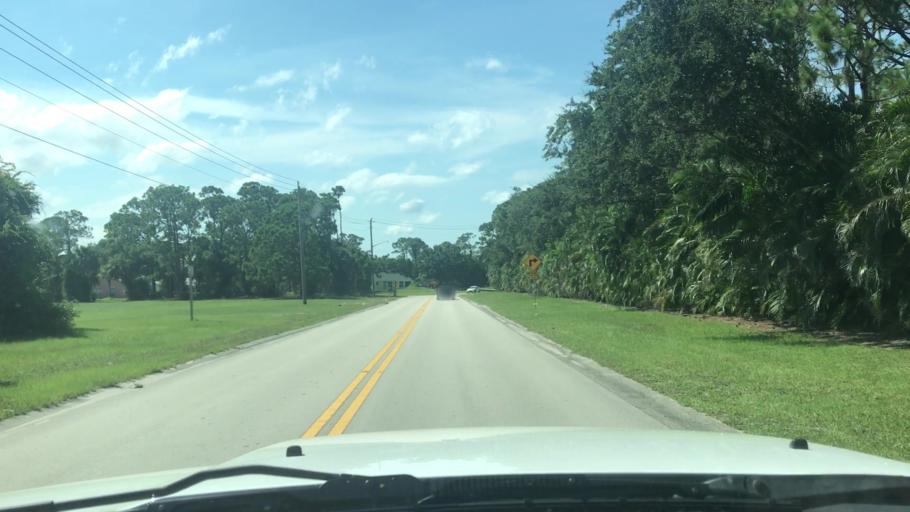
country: US
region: Florida
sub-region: Indian River County
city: Florida Ridge
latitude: 27.5630
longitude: -80.3972
